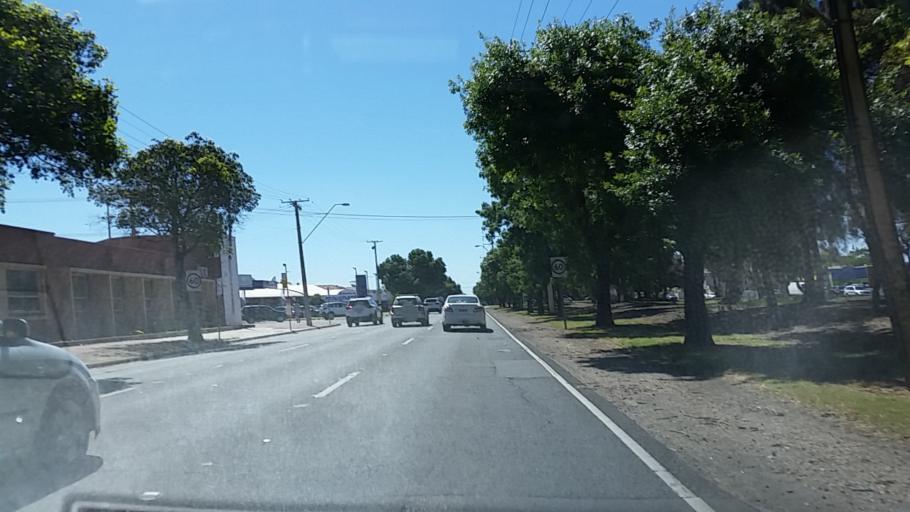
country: AU
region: South Australia
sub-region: Charles Sturt
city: Woodville
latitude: -34.8851
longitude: 138.5415
